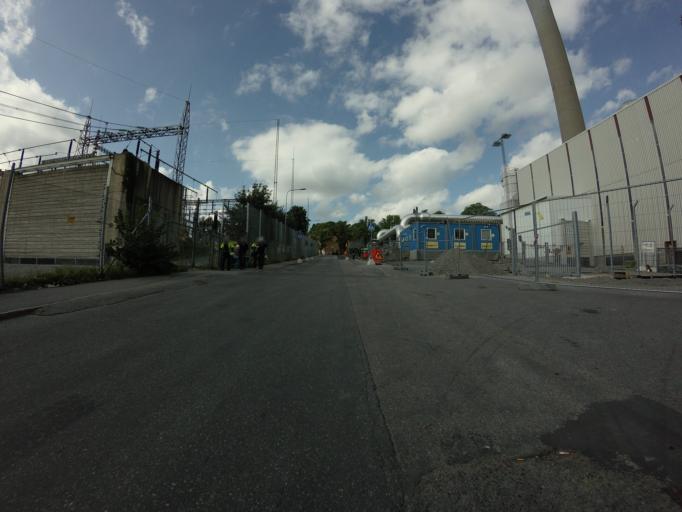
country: SE
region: Stockholm
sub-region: Stockholms Kommun
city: OEstermalm
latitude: 59.3527
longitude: 18.0998
